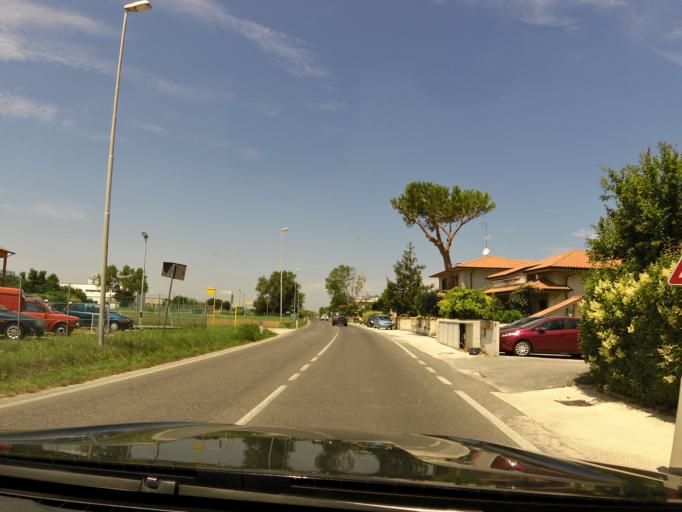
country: IT
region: The Marches
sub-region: Provincia di Pesaro e Urbino
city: Marotta
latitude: 43.7899
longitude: 13.1059
